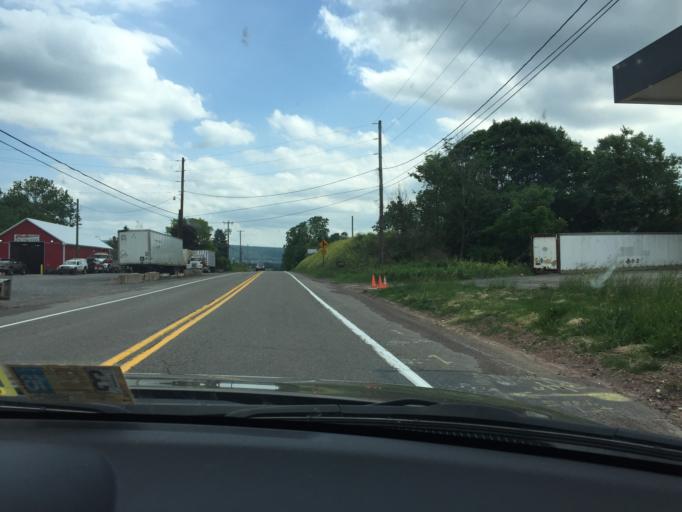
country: US
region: Pennsylvania
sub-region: Luzerne County
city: Conyngham
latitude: 41.0228
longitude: -76.0792
